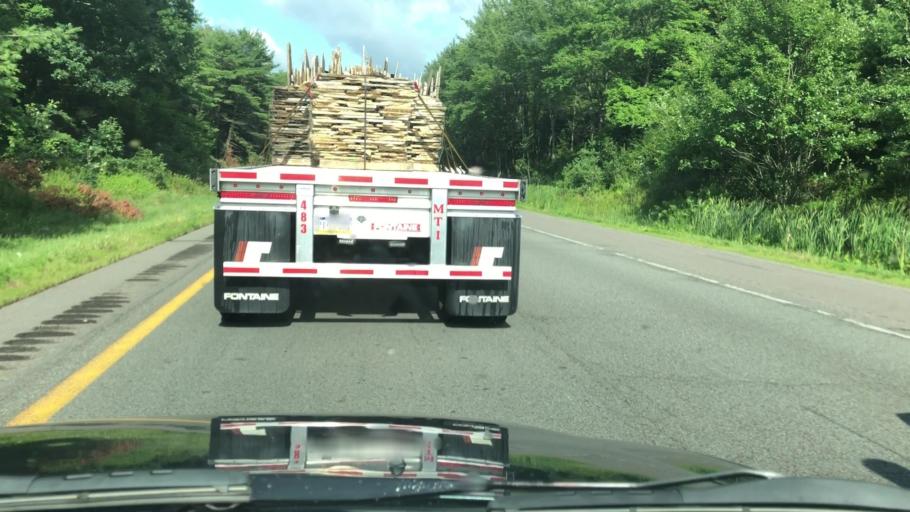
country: US
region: Pennsylvania
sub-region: Pike County
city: Hemlock Farms
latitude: 41.3565
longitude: -75.0846
